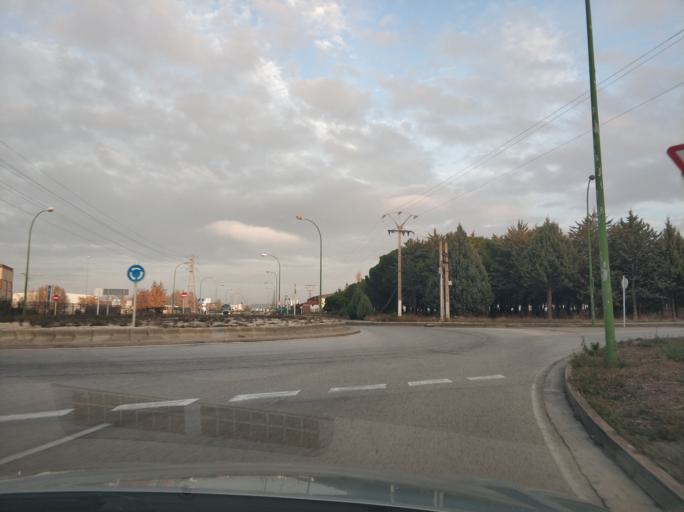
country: ES
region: Castille and Leon
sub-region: Provincia de Burgos
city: Villalbilla de Burgos
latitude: 42.3679
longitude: -3.7458
